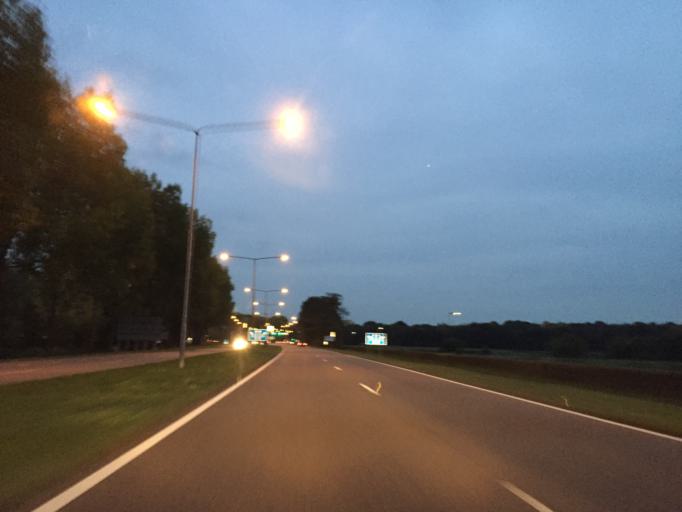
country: NL
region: North Brabant
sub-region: Gemeente 's-Hertogenbosch
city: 's-Hertogenbosch
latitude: 51.6929
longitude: 5.2559
